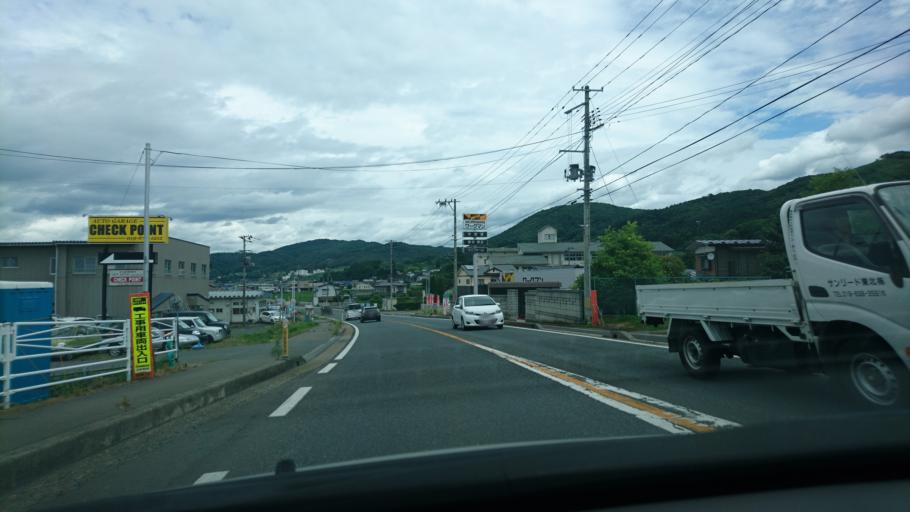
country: JP
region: Iwate
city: Morioka-shi
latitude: 39.6381
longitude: 141.1862
